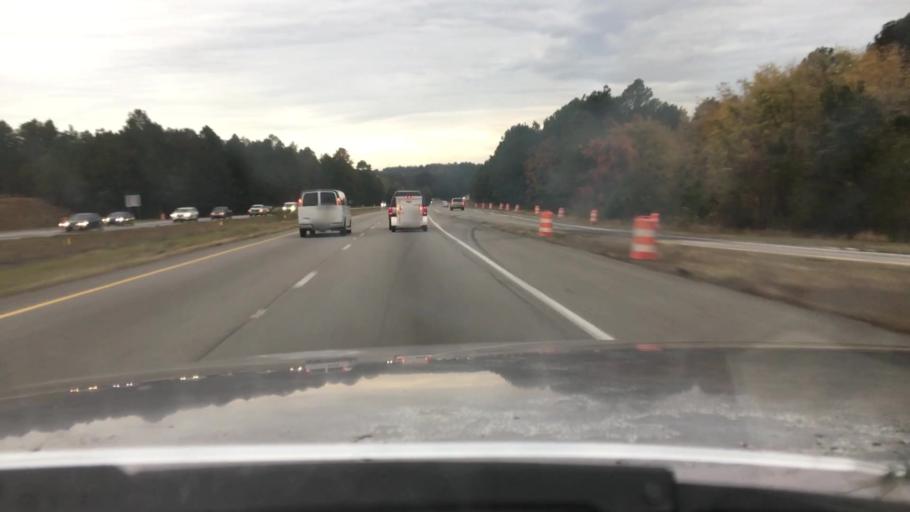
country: US
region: South Carolina
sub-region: Lexington County
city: Red Bank
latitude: 33.9255
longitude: -81.2929
